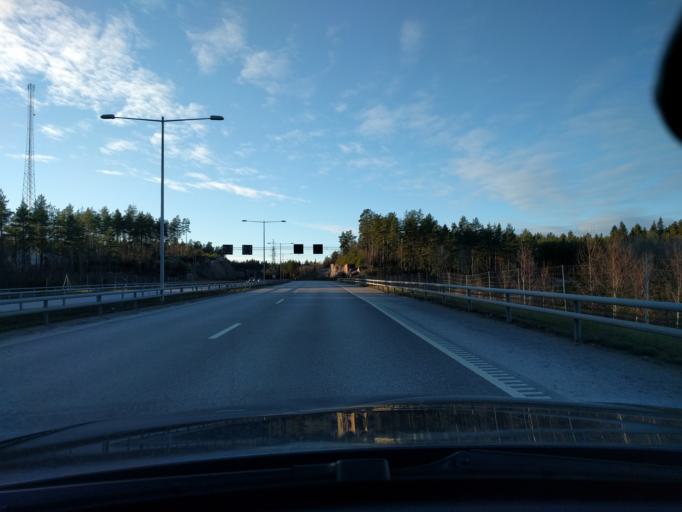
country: SE
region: Stockholm
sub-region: Sollentuna Kommun
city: Sollentuna
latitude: 59.4665
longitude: 17.9765
